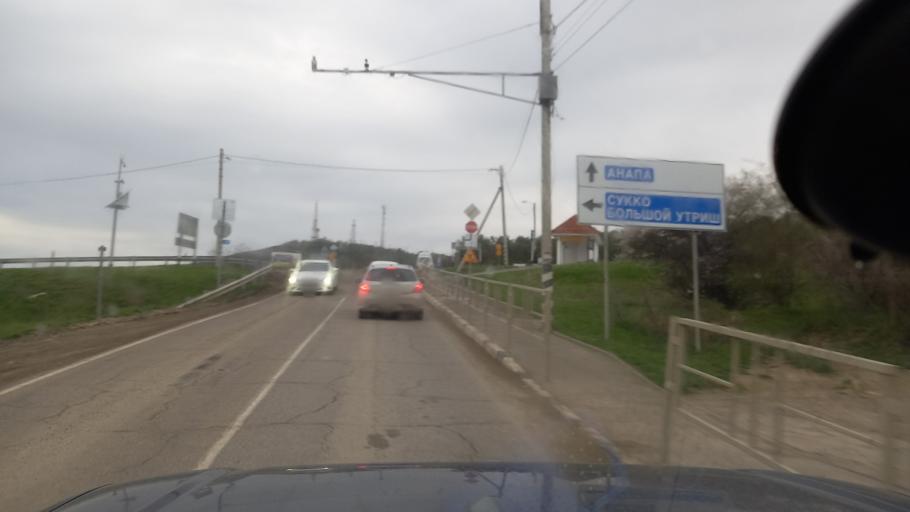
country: RU
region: Krasnodarskiy
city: Anapskaya
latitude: 44.8435
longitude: 37.3797
